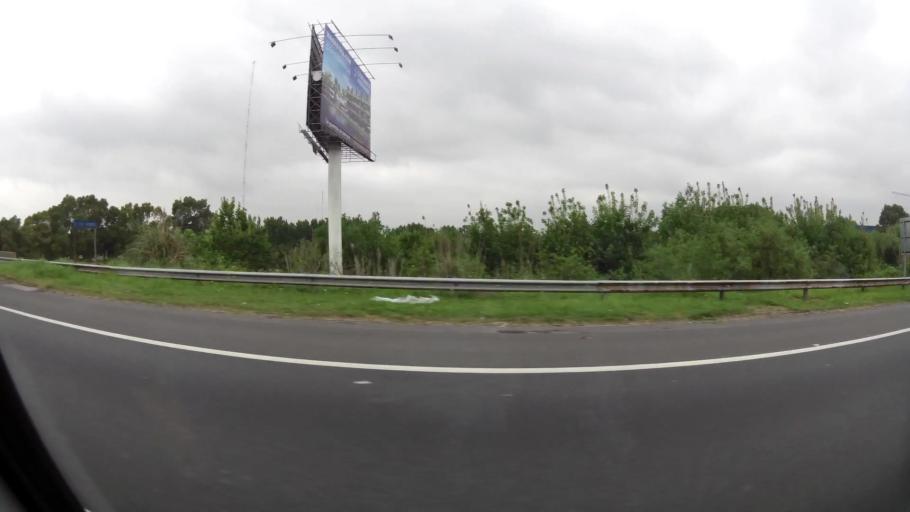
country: AR
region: Buenos Aires
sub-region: Partido de Avellaneda
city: Avellaneda
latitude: -34.6812
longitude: -58.3167
